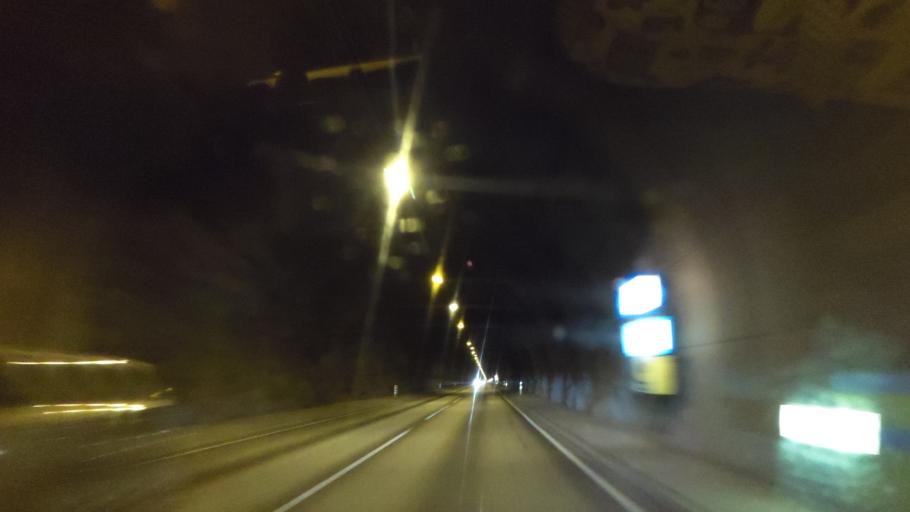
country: IS
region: Capital Region
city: Reykjavik
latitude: 64.2874
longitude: -21.8370
